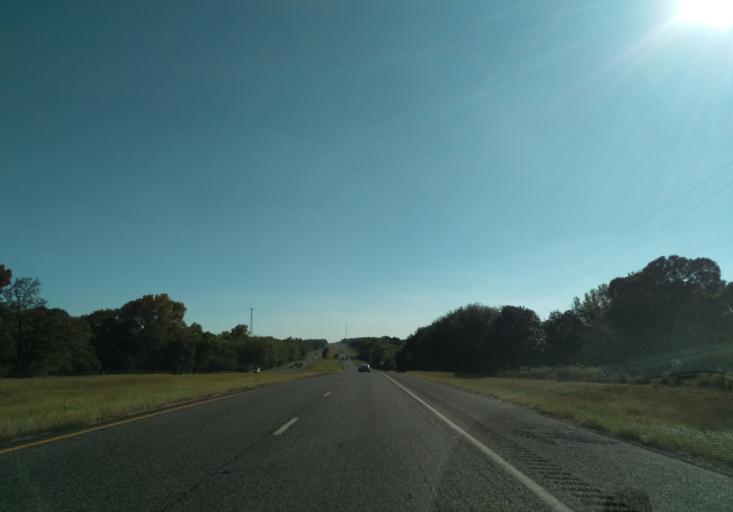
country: US
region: Texas
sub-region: Waller County
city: Hempstead
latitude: 30.1924
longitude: -96.0622
